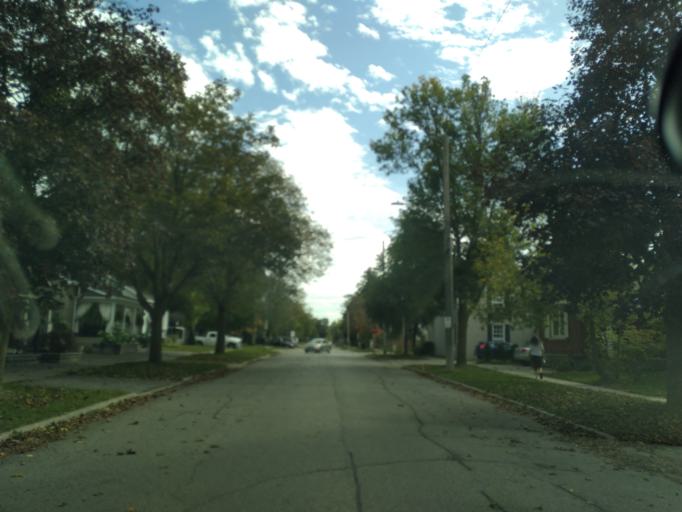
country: CA
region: Ontario
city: Newmarket
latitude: 43.9994
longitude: -79.4637
